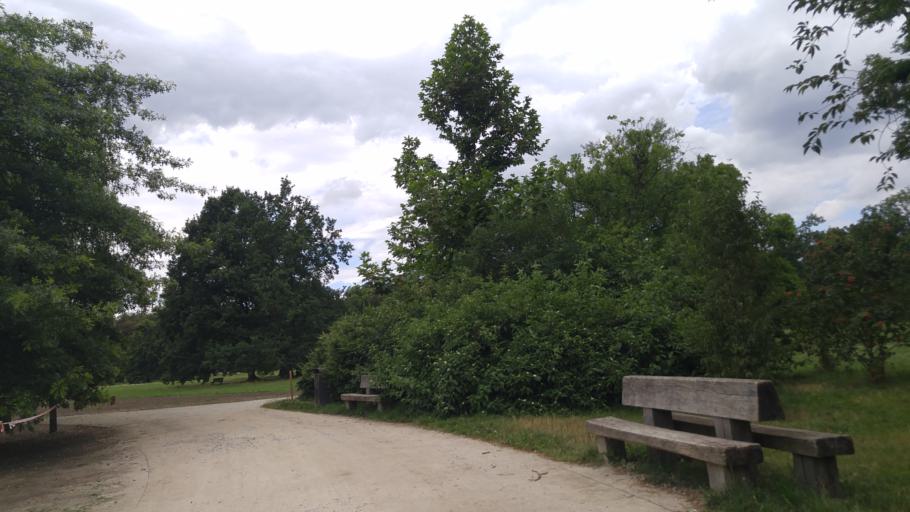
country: CZ
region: Praha
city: Prague
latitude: 50.1074
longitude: 14.4219
